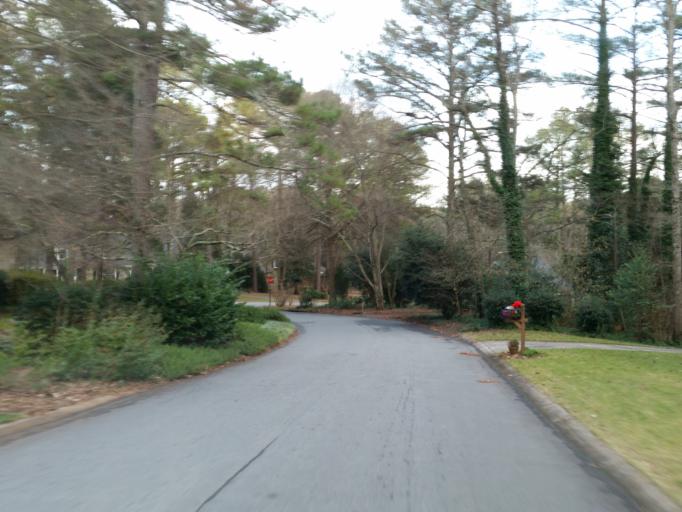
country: US
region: Georgia
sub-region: Cobb County
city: Marietta
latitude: 33.9950
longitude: -84.4908
